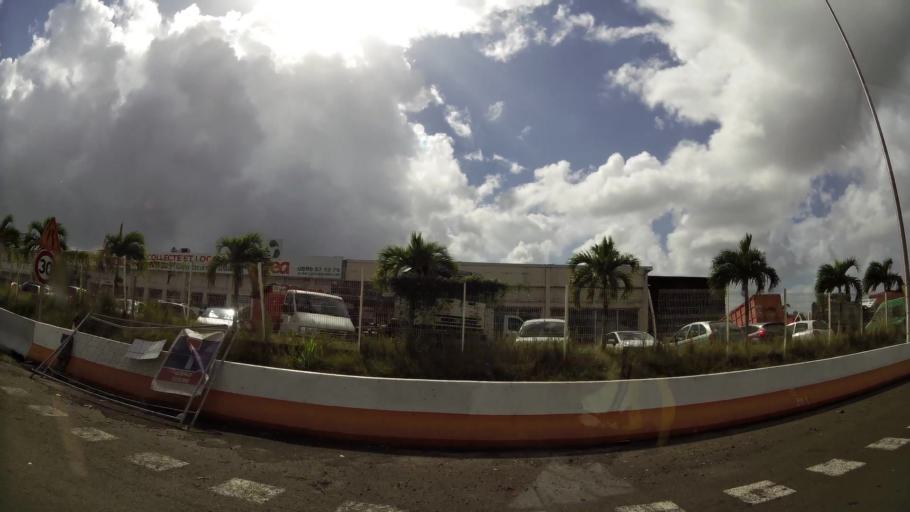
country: MQ
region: Martinique
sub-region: Martinique
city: Le Lamentin
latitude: 14.6105
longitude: -61.0067
